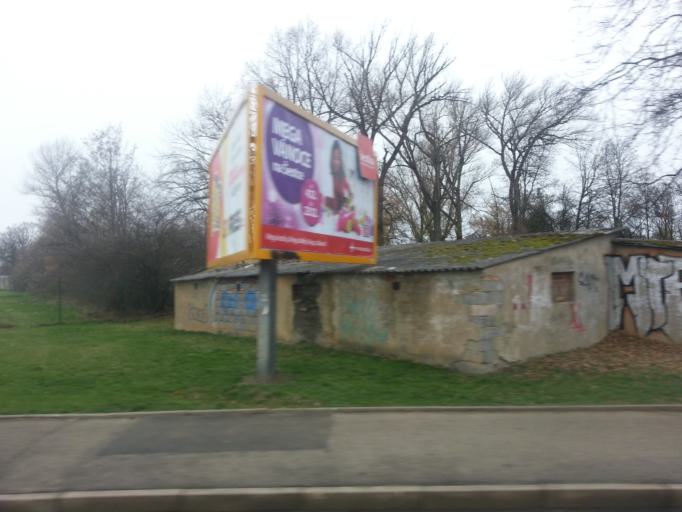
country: CZ
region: Central Bohemia
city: Hostivice
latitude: 50.0949
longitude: 14.2935
